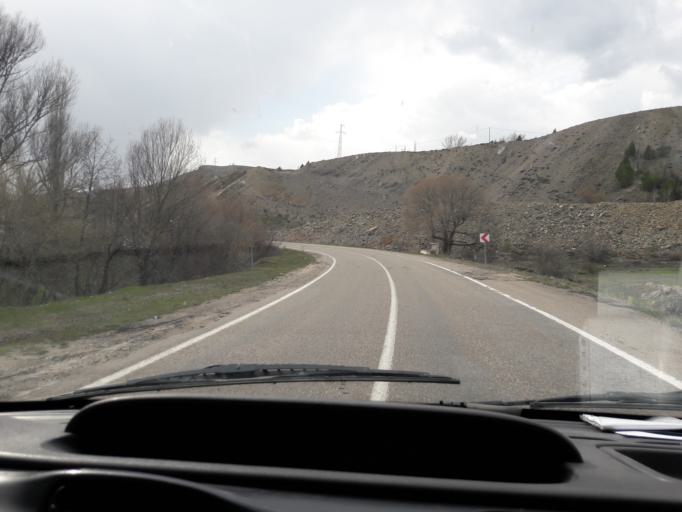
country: TR
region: Giresun
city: Alucra
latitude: 40.2717
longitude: 38.8826
